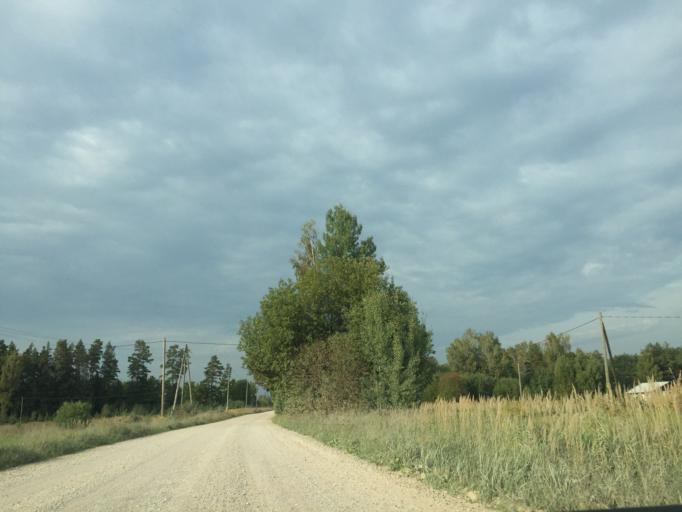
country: LV
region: Ikskile
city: Ikskile
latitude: 56.8120
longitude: 24.4475
